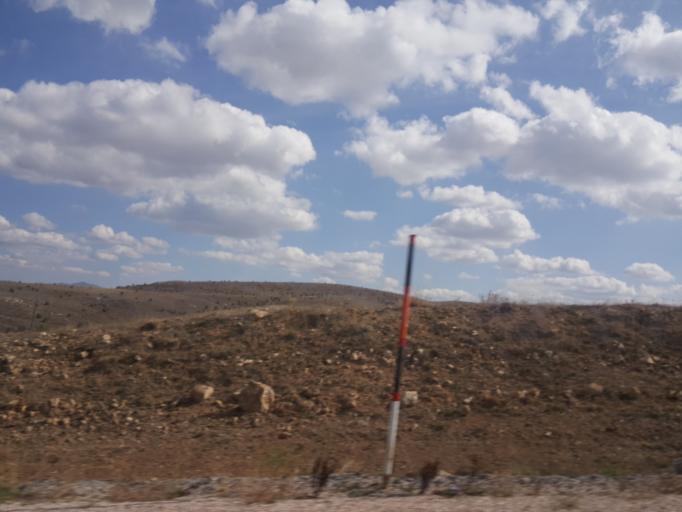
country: TR
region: Tokat
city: Camlibel
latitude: 40.1547
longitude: 36.4000
